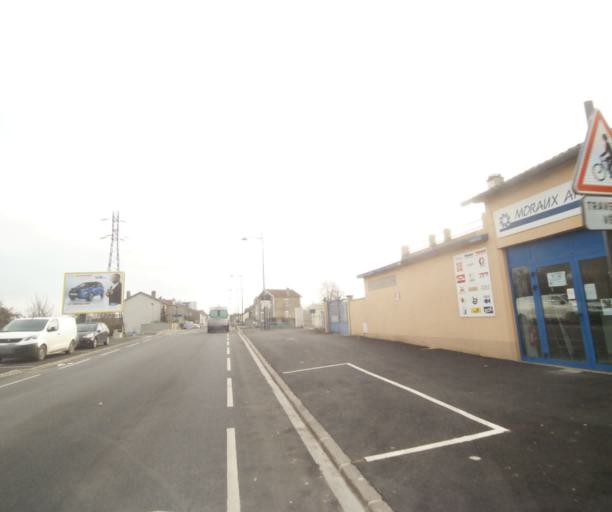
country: FR
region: Champagne-Ardenne
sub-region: Departement de la Haute-Marne
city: Saint-Dizier
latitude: 48.6387
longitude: 4.9261
